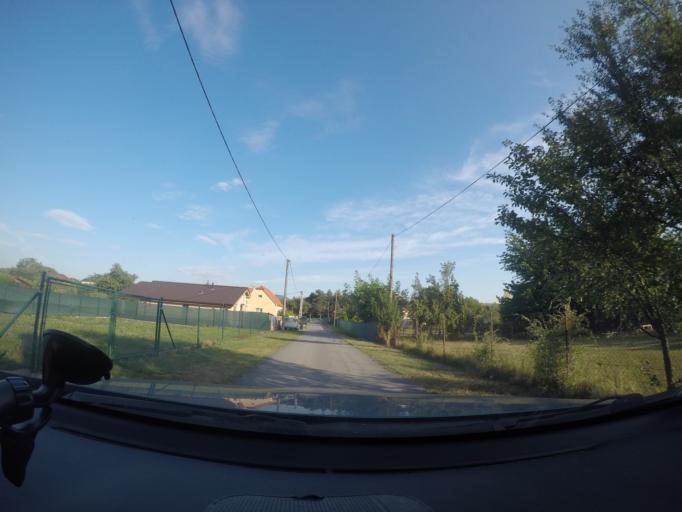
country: SK
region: Trenciansky
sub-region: Okres Trencin
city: Trencin
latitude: 48.8762
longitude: 18.0079
